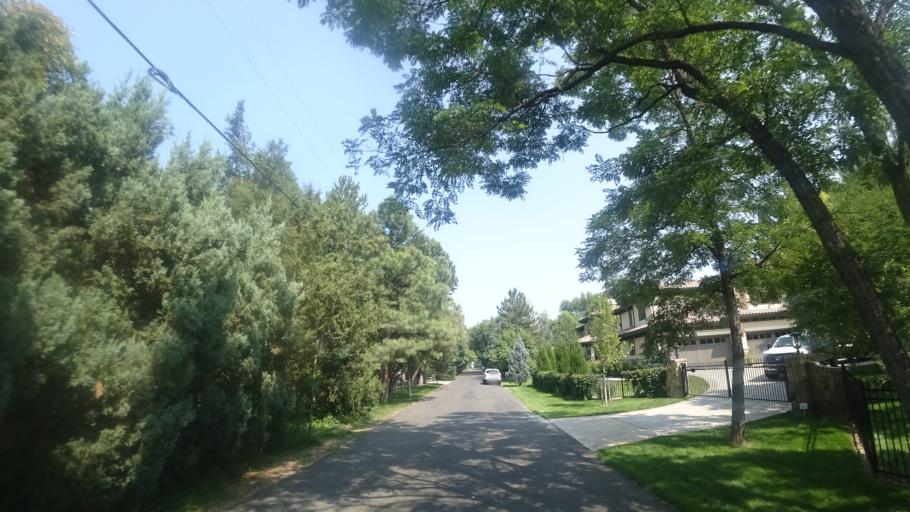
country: US
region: Colorado
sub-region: Arapahoe County
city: Cherry Hills Village
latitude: 39.6332
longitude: -104.9725
